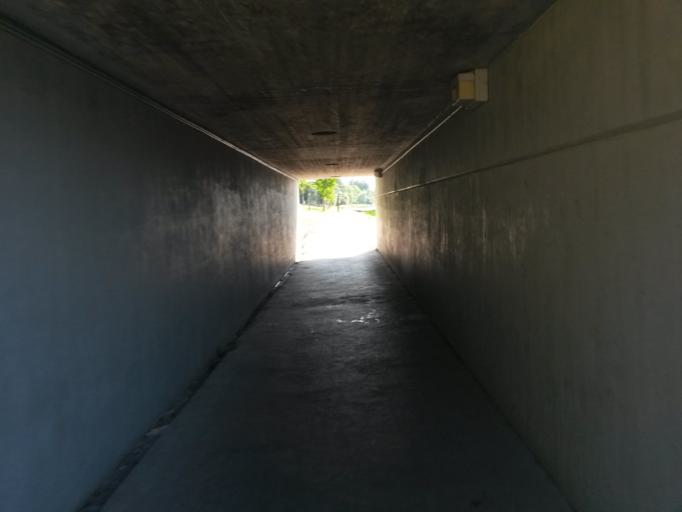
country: SE
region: Vaestra Goetaland
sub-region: Lidkopings Kommun
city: Lidkoping
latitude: 58.5006
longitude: 13.1581
